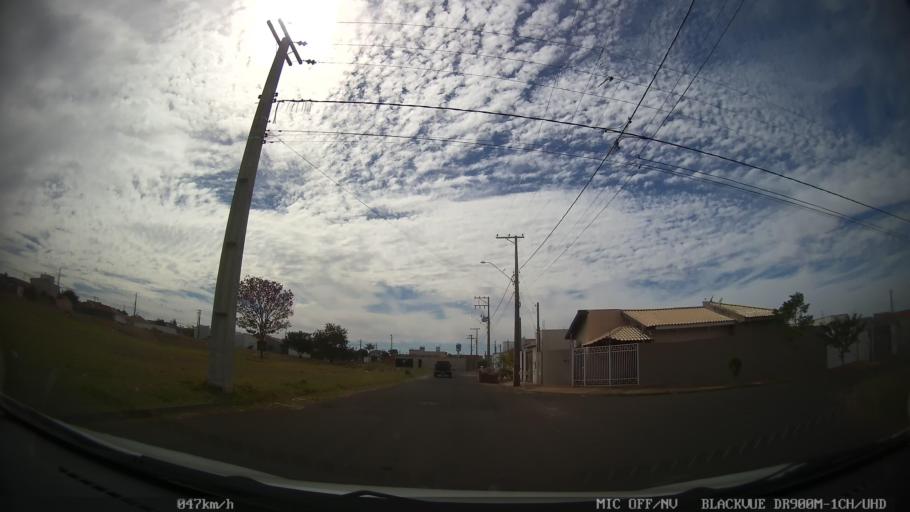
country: BR
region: Sao Paulo
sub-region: Catanduva
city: Catanduva
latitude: -21.1683
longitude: -48.9672
